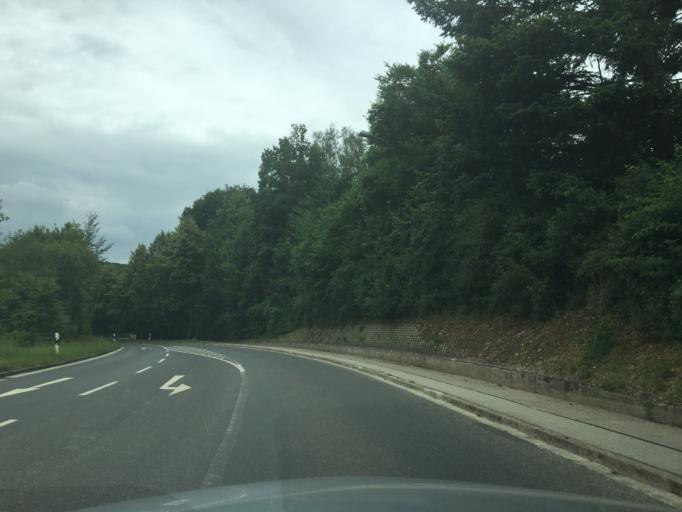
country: DE
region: Bavaria
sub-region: Regierungsbezirk Mittelfranken
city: Greding
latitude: 49.0445
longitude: 11.3621
